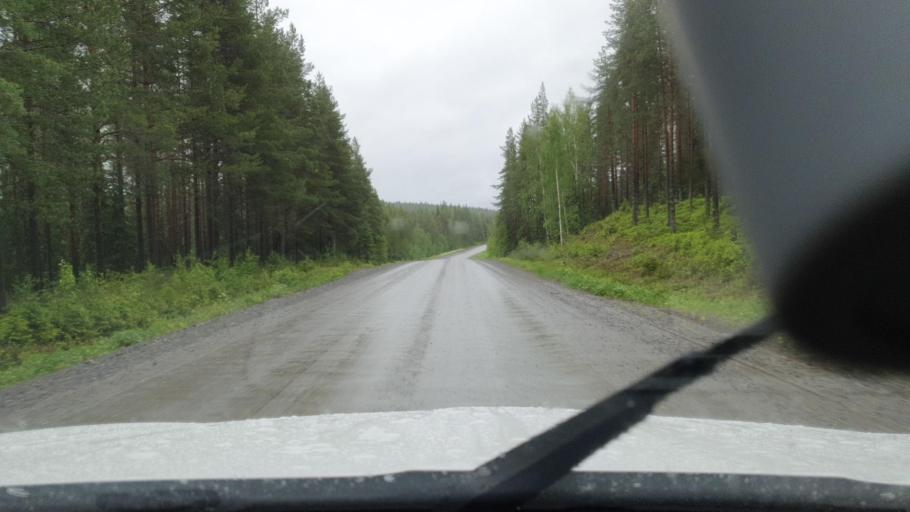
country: SE
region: Vaesterbotten
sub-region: Skelleftea Kommun
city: Burtraesk
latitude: 64.3800
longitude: 20.3399
